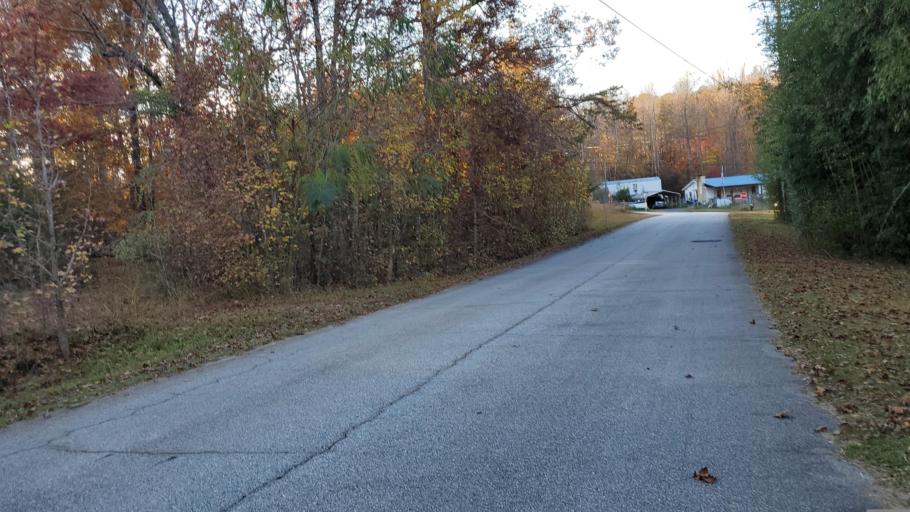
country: US
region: South Carolina
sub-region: Greenville County
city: Tigerville
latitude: 35.0712
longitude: -82.3292
